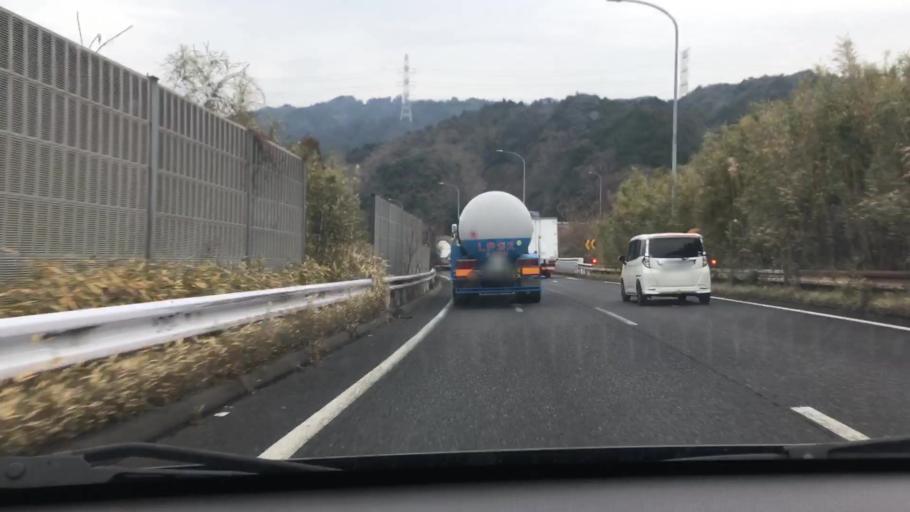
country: JP
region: Mie
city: Kameyama
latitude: 34.8364
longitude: 136.3358
